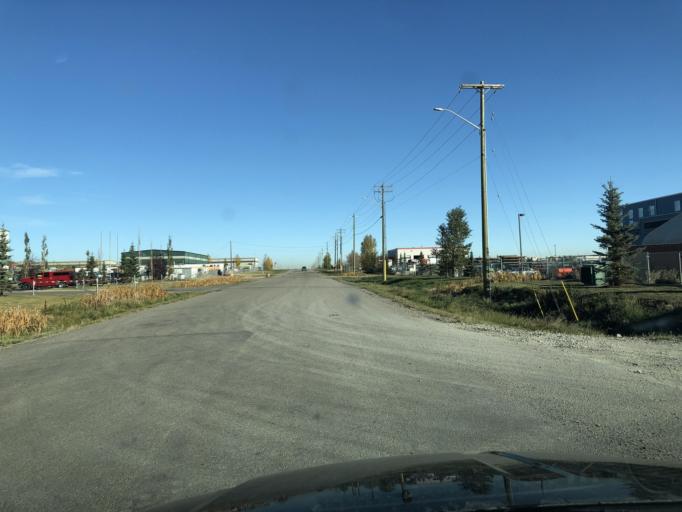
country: CA
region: Alberta
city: Chestermere
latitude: 50.9632
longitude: -113.9026
